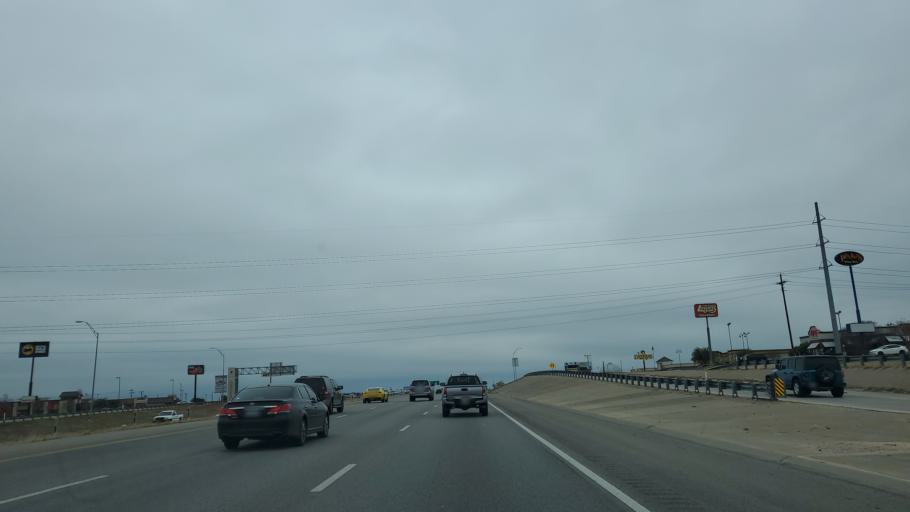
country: US
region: Texas
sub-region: Bell County
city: Killeen
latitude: 31.0881
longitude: -97.7144
